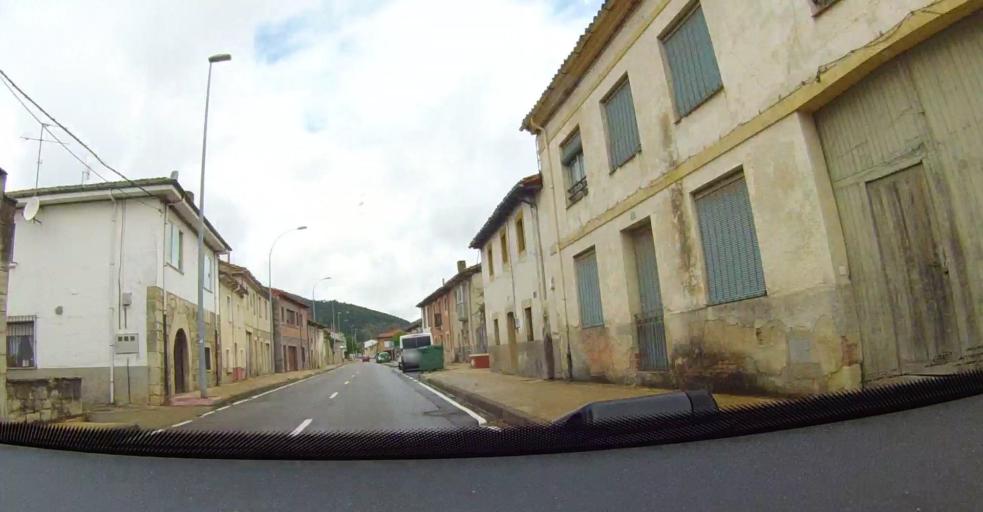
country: ES
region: Castille and Leon
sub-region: Provincia de Leon
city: Bonar
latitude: 42.8702
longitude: -5.3223
